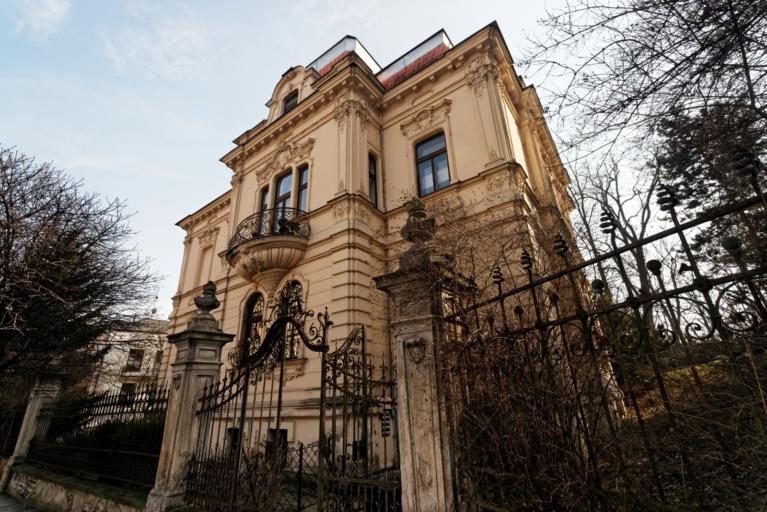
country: CZ
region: Olomoucky
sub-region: Okres Olomouc
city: Olomouc
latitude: 49.5891
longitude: 17.2509
